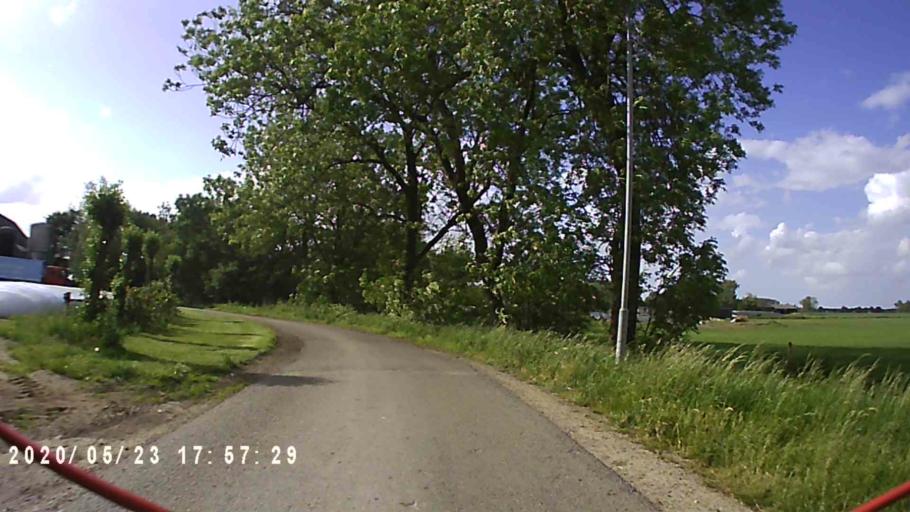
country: NL
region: Groningen
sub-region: Gemeente Slochteren
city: Slochteren
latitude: 53.2523
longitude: 6.7413
